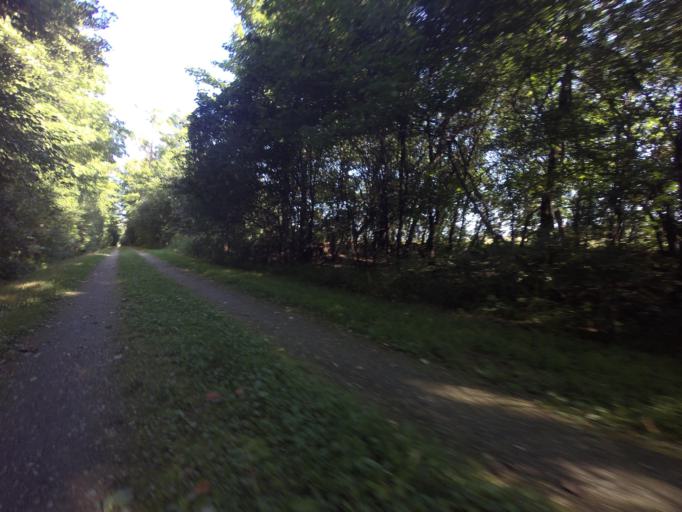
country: CA
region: Ontario
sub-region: Wellington County
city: Guelph
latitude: 43.6557
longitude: -80.4227
